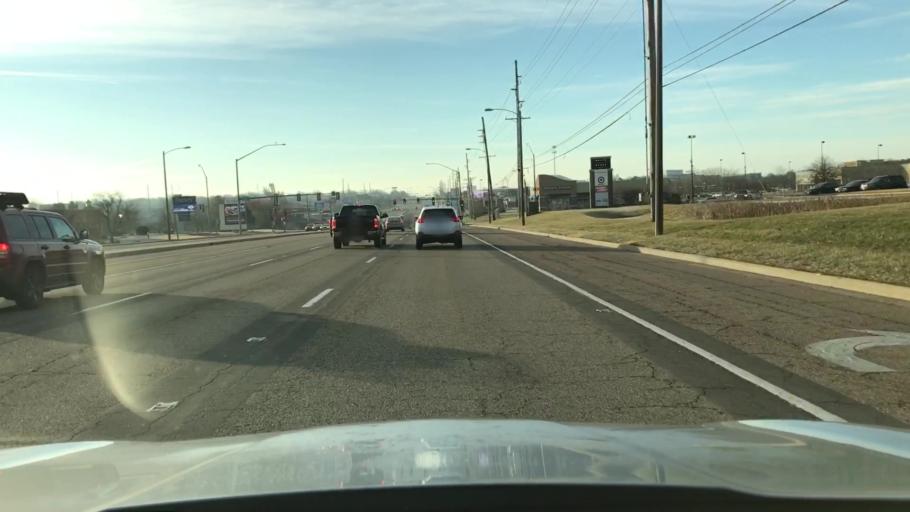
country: US
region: Illinois
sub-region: McLean County
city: Normal
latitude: 40.5081
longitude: -88.9534
